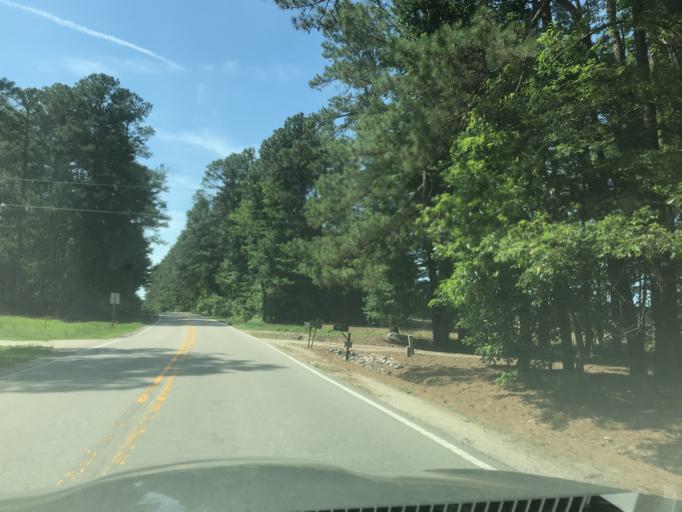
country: US
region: North Carolina
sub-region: Wake County
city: Wendell
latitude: 35.7673
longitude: -78.3540
